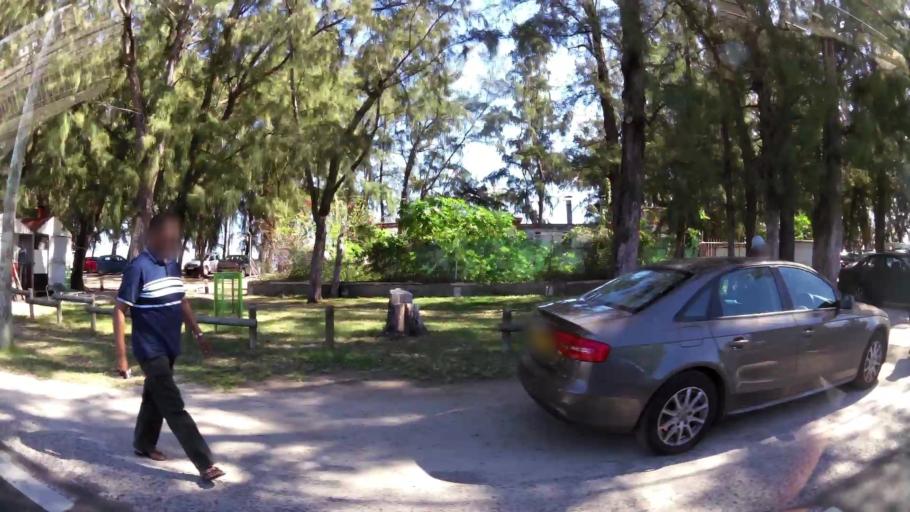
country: MU
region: Black River
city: Flic en Flac
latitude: -20.2808
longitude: 57.3660
